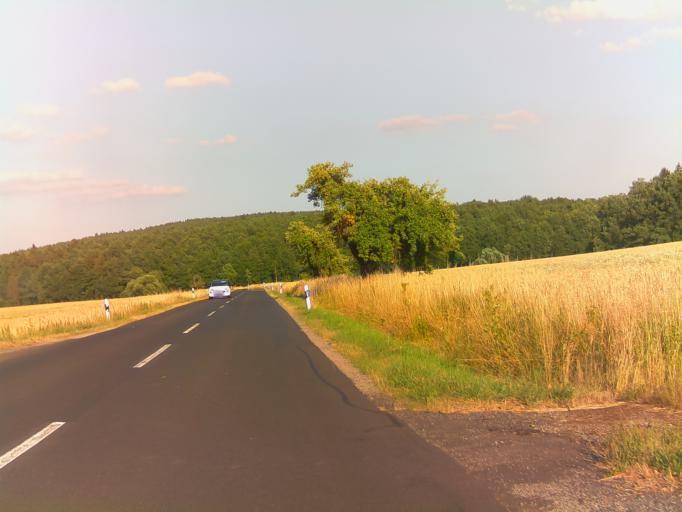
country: DE
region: Bavaria
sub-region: Regierungsbezirk Unterfranken
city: Oberelsbach
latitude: 50.4231
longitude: 10.1130
